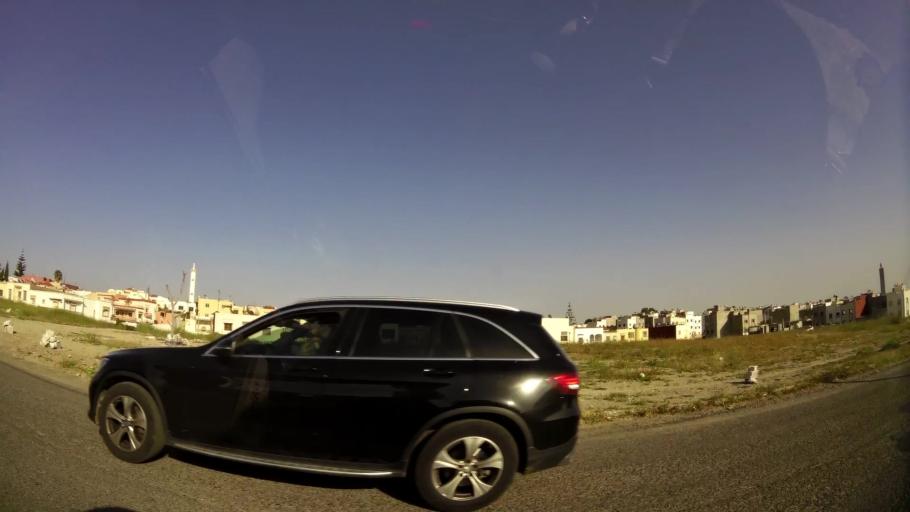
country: MA
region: Souss-Massa-Draa
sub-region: Agadir-Ida-ou-Tnan
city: Agadir
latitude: 30.4274
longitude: -9.5752
